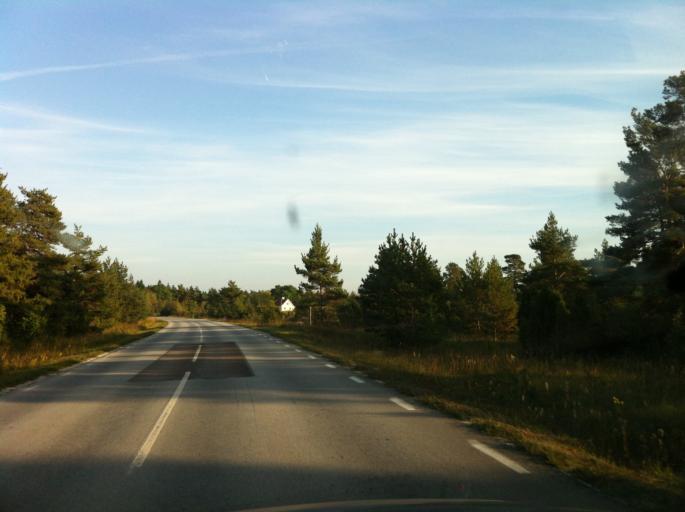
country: SE
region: Gotland
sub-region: Gotland
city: Slite
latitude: 57.4284
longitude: 18.7625
